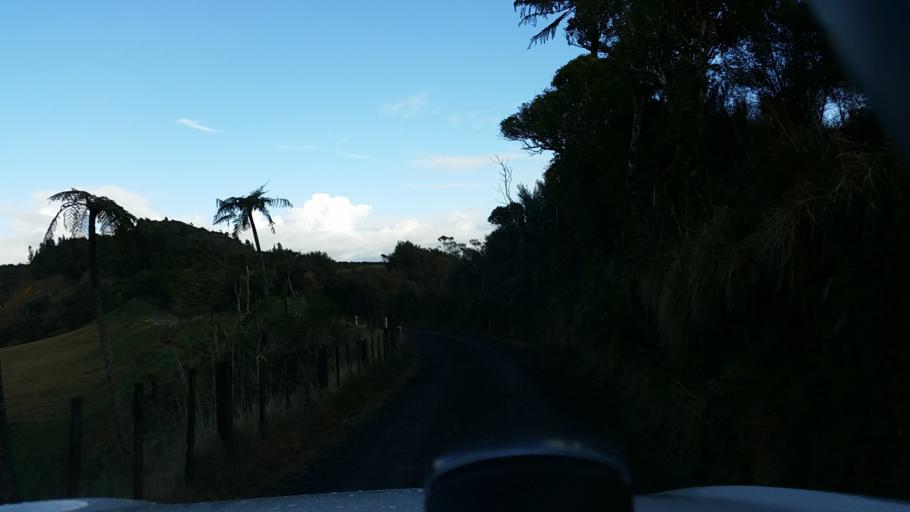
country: NZ
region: Taranaki
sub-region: South Taranaki District
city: Eltham
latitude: -39.4134
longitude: 174.5650
